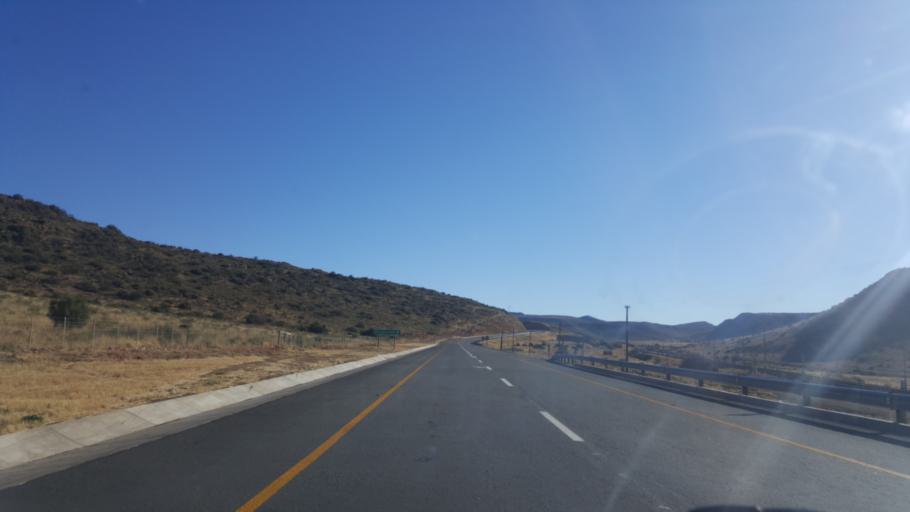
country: ZA
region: Eastern Cape
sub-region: Chris Hani District Municipality
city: Middelburg
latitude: -31.3859
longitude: 25.0315
